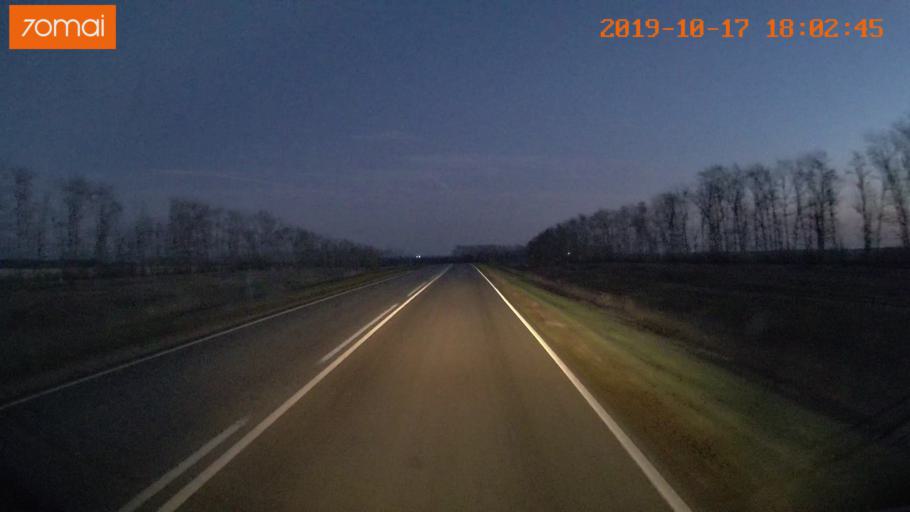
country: RU
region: Tula
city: Kurkino
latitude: 53.5033
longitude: 38.6174
